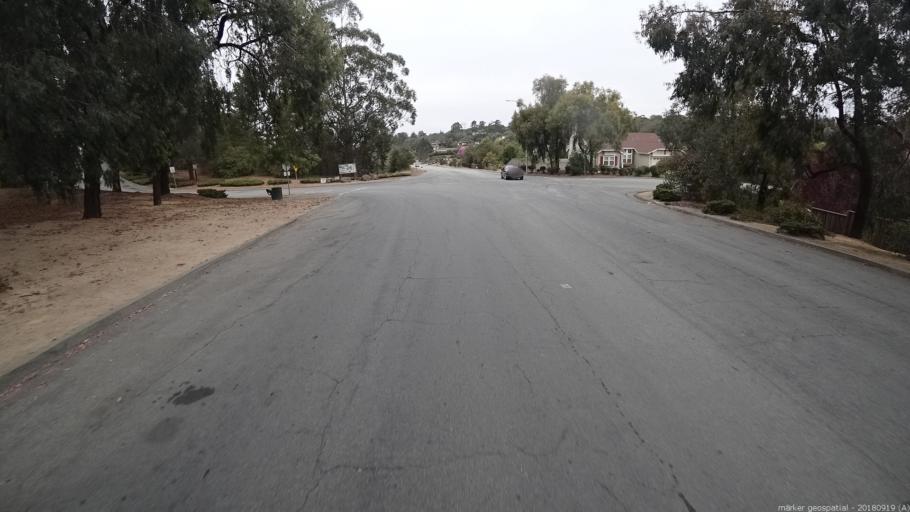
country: US
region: California
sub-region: Monterey County
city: Castroville
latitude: 36.7775
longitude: -121.7159
